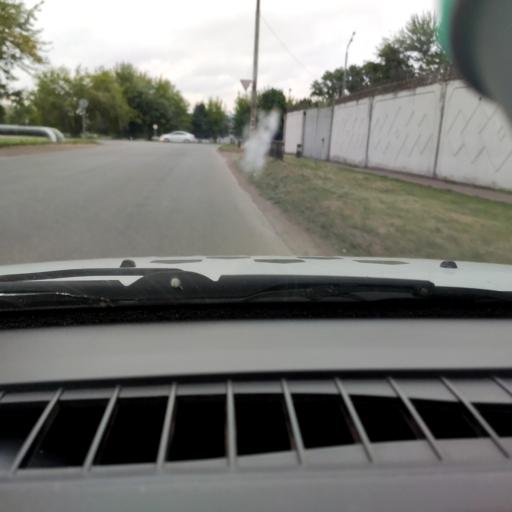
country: RU
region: Tatarstan
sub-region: Tukayevskiy Rayon
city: Naberezhnyye Chelny
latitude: 55.6663
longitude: 52.2740
